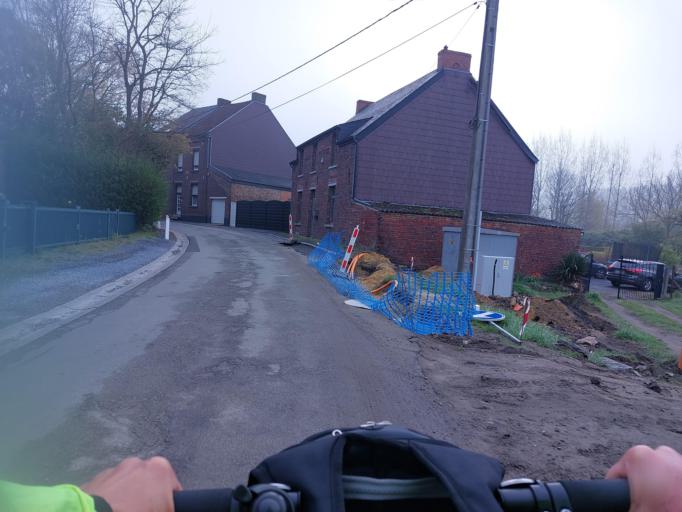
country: BE
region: Wallonia
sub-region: Province du Hainaut
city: Roeulx
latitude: 50.4674
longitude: 4.0381
